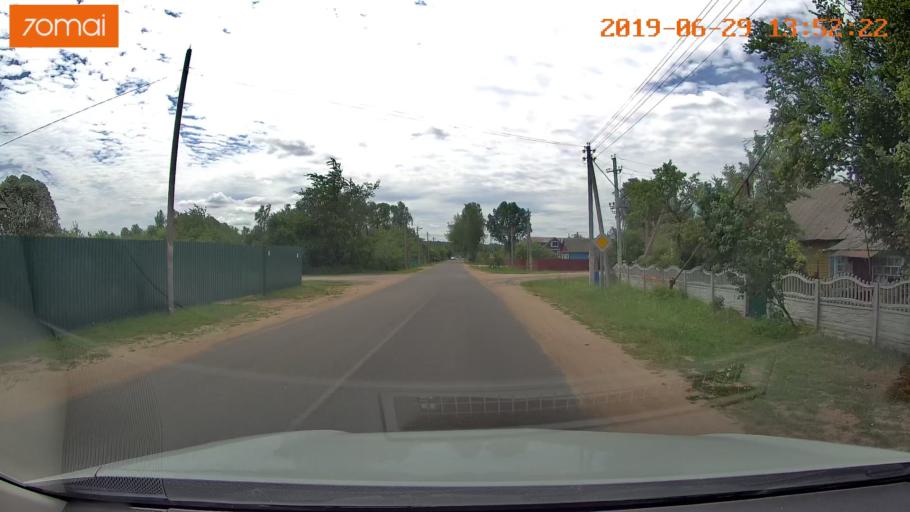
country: BY
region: Minsk
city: Slutsk
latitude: 52.9959
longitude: 27.5556
